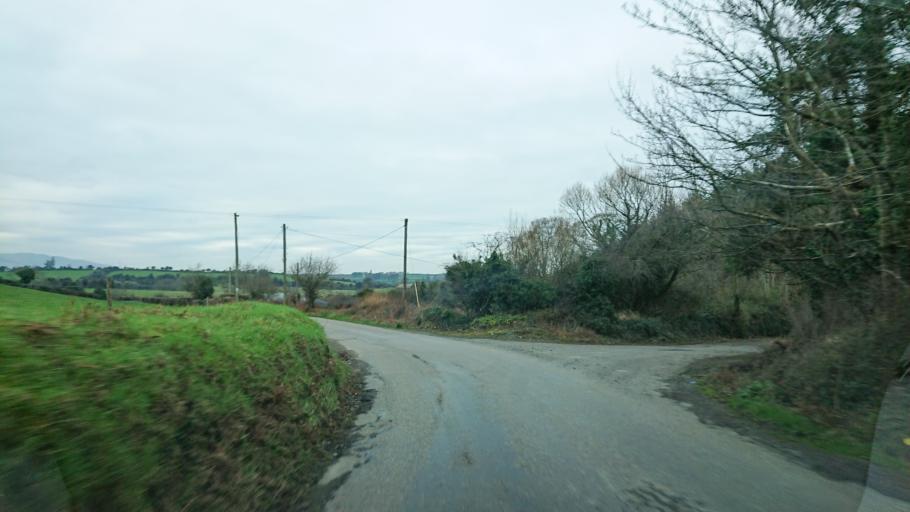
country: IE
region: Munster
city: Carrick-on-Suir
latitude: 52.2754
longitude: -7.4110
